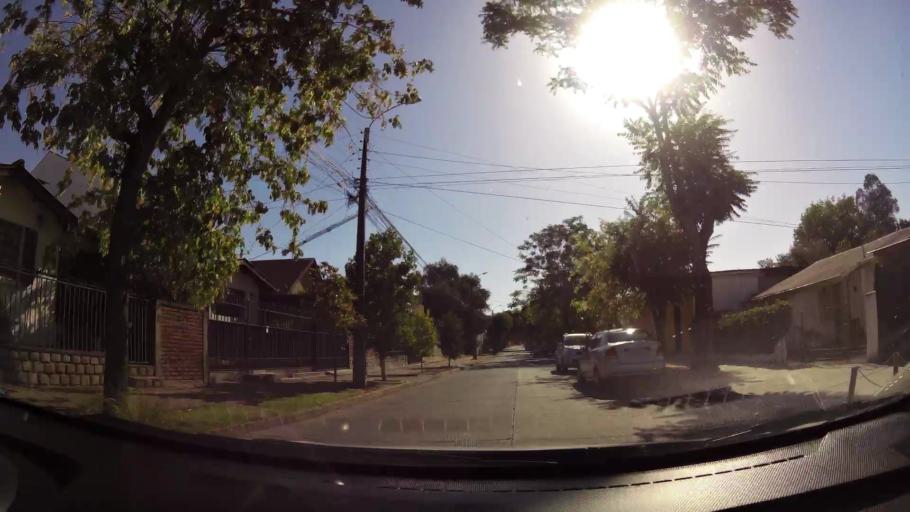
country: CL
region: Maule
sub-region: Provincia de Talca
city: Talca
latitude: -35.4267
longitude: -71.6720
